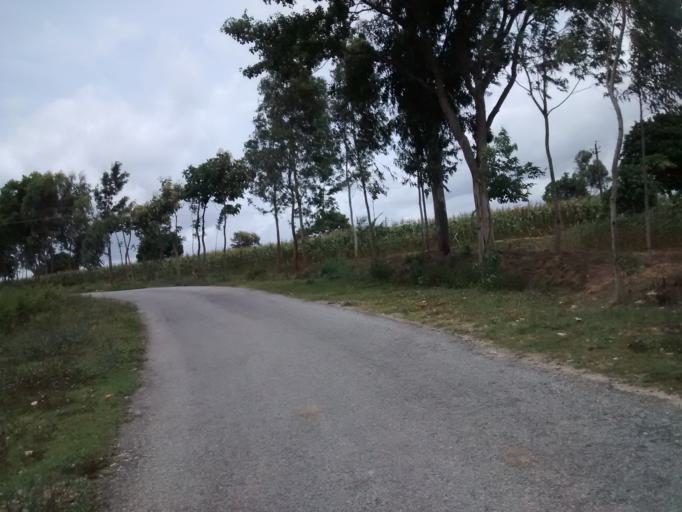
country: IN
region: Karnataka
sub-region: Hassan
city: Hassan
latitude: 12.9249
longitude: 76.1377
